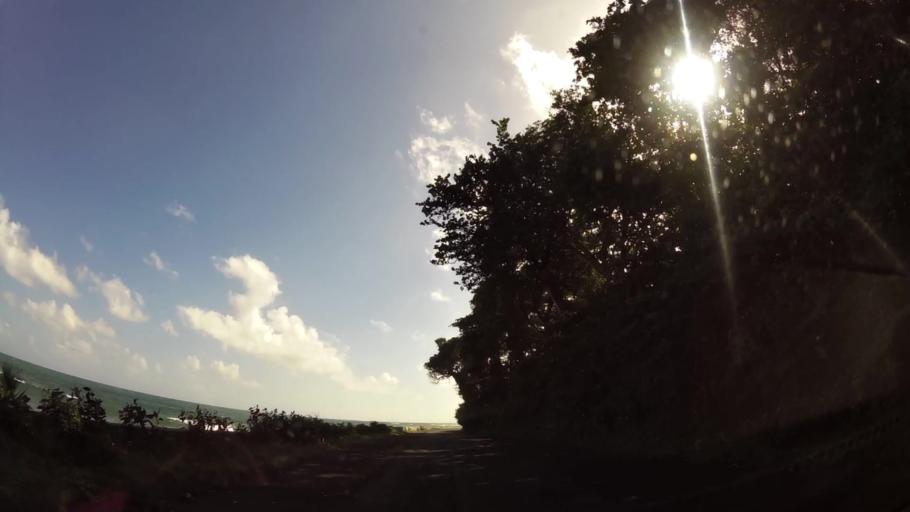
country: DM
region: Saint Andrew
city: Marigot
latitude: 15.5448
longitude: -61.2896
